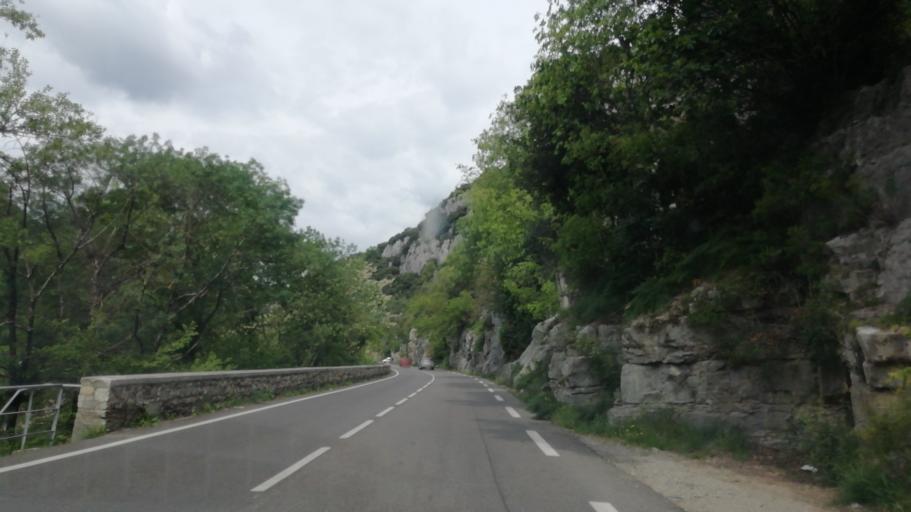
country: FR
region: Languedoc-Roussillon
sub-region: Departement de l'Herault
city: Laroque
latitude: 43.9156
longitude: 3.7363
